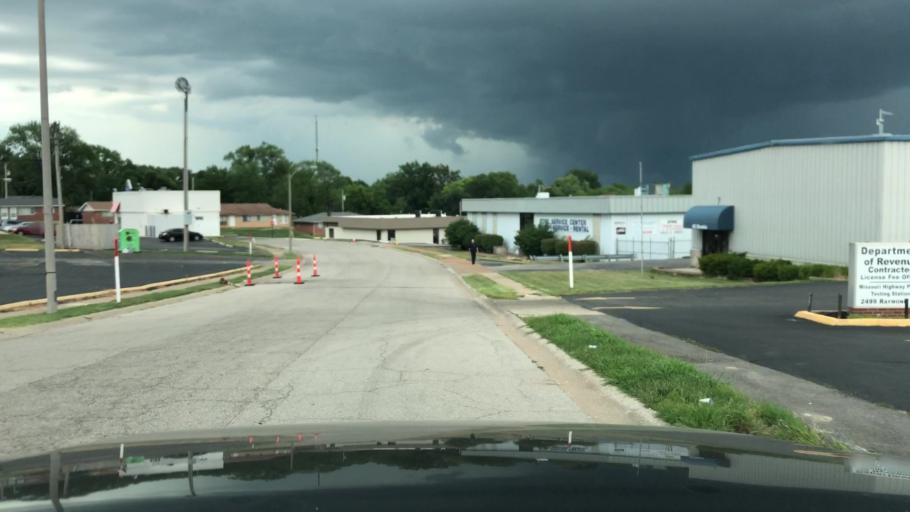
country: US
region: Missouri
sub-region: Saint Charles County
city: Saint Charles
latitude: 38.7868
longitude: -90.5133
